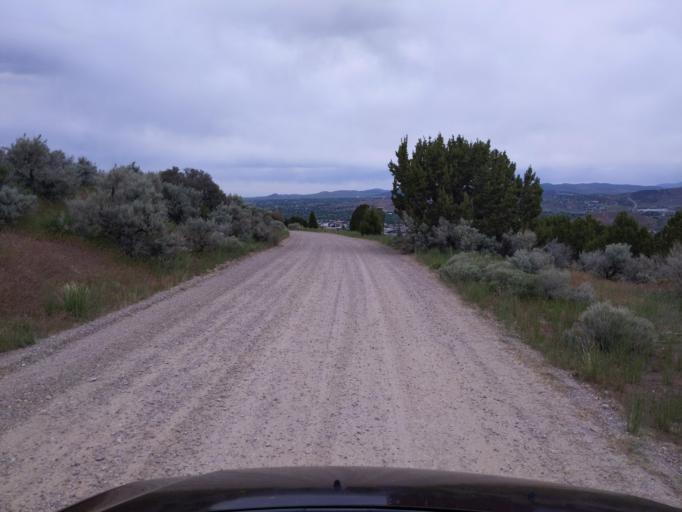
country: US
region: Idaho
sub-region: Bannock County
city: Pocatello
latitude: 42.8441
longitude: -112.4591
